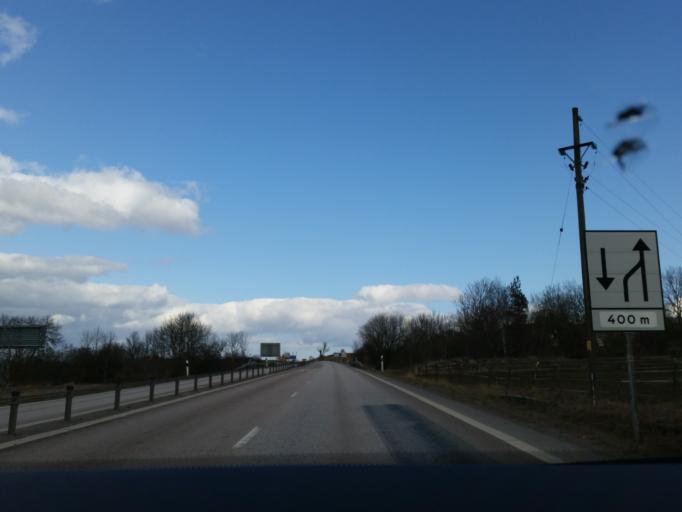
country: SE
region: Kalmar
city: Faerjestaden
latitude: 56.6754
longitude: 16.5185
